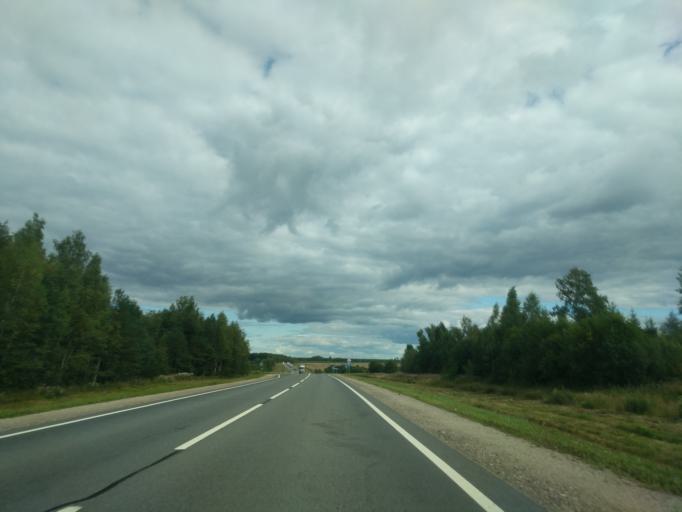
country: RU
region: Kostroma
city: Sudislavl'
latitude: 57.8180
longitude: 41.9393
